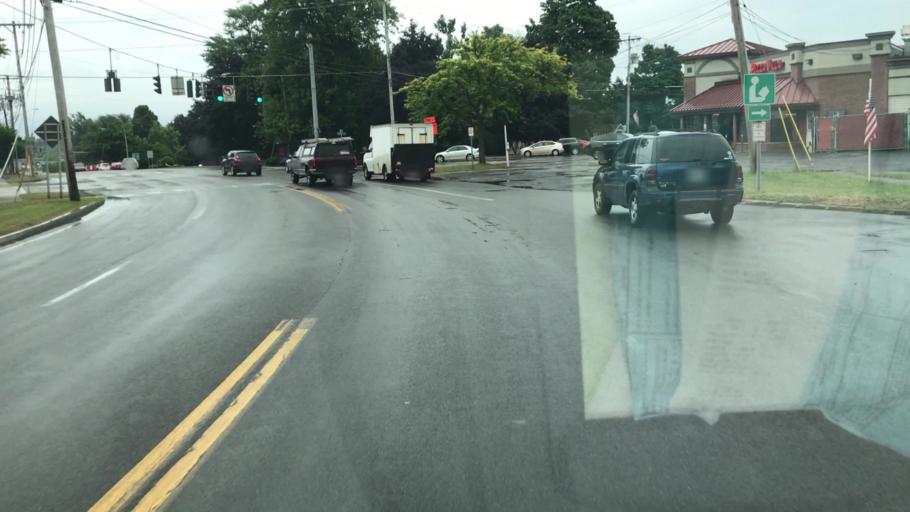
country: US
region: New York
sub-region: Onondaga County
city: Liverpool
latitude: 43.1047
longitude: -76.2082
